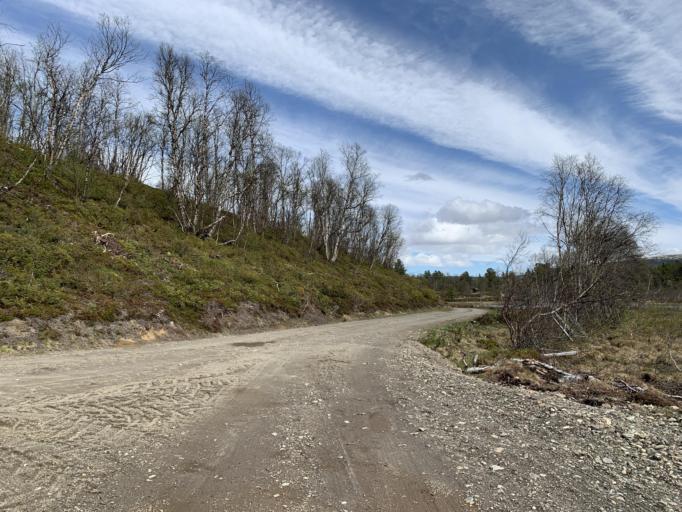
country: NO
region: Hedmark
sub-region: Alvdal
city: Alvdal
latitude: 62.4132
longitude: 10.4037
